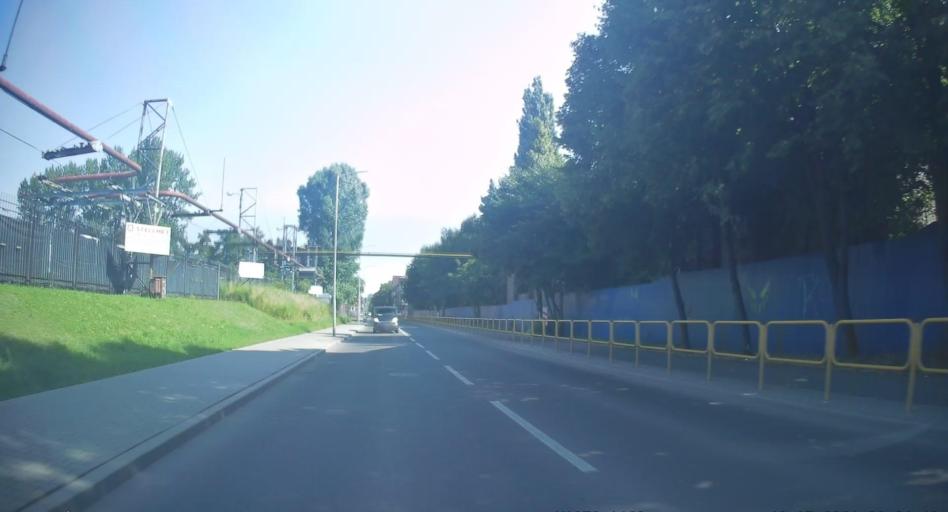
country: PL
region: Silesian Voivodeship
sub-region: Swietochlowice
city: Swietochlowice
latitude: 50.2865
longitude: 18.9138
